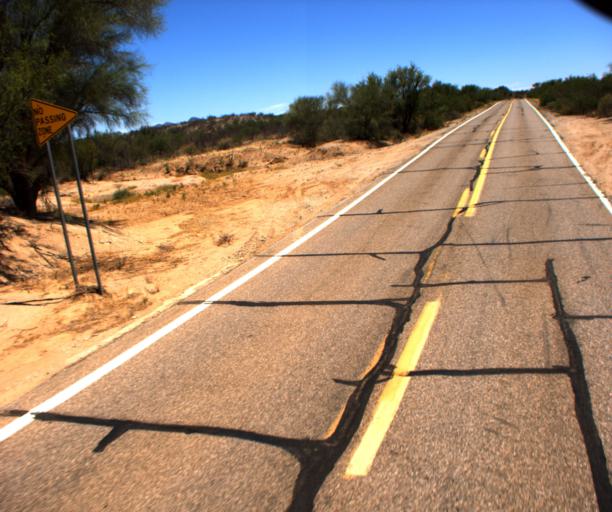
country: US
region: Arizona
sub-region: Pima County
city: Three Points
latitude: 31.9233
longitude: -111.3907
